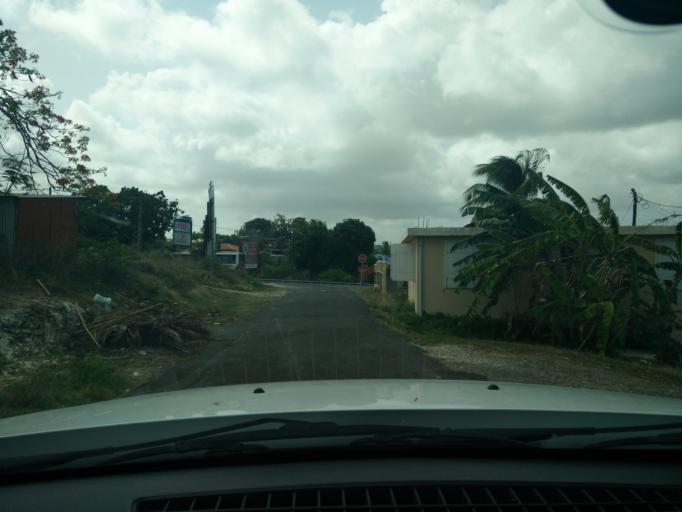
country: GP
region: Guadeloupe
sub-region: Guadeloupe
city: Sainte-Anne
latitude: 16.2161
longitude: -61.4333
